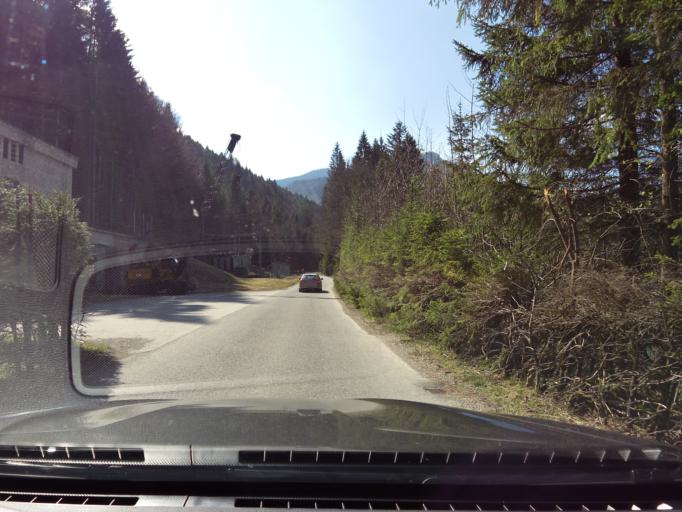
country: DE
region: Bavaria
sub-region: Upper Bavaria
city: Wallgau
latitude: 47.5688
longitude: 11.3090
